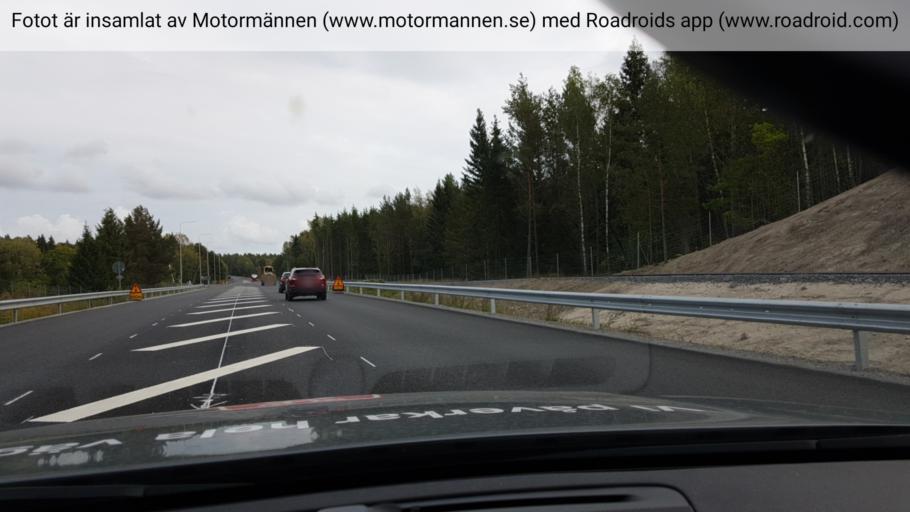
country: SE
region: Stockholm
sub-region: Norrtalje Kommun
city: Bjorko
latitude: 59.7215
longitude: 18.9107
